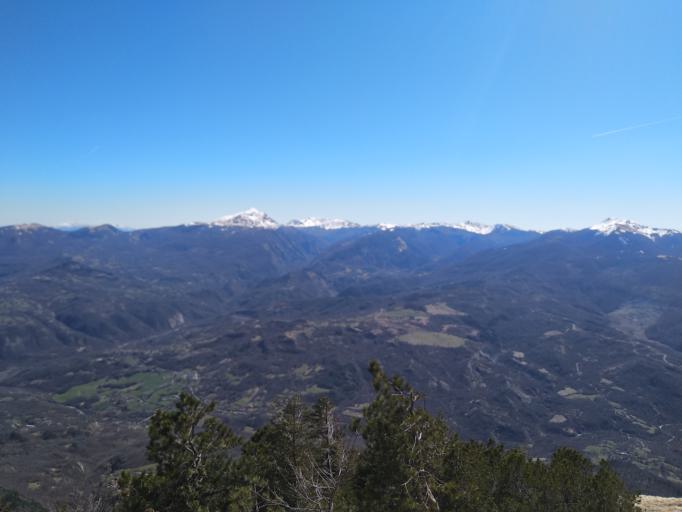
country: IT
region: Emilia-Romagna
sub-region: Provincia di Reggio Emilia
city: Collagna
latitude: 44.3726
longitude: 10.2853
